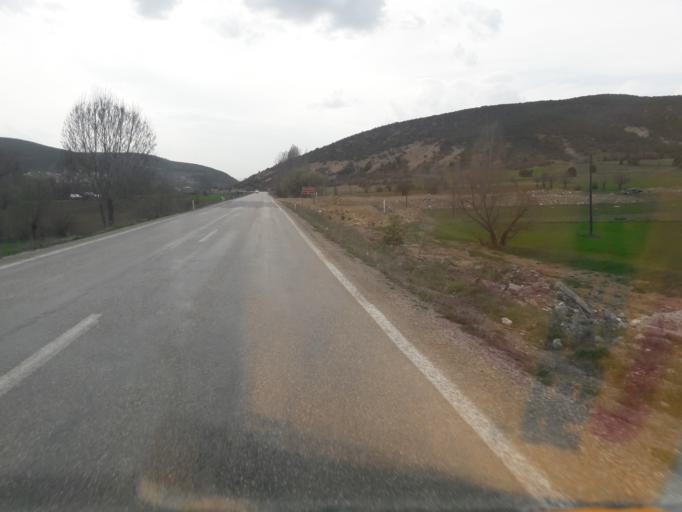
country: TR
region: Gumushane
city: Siran
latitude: 40.1771
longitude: 39.1468
